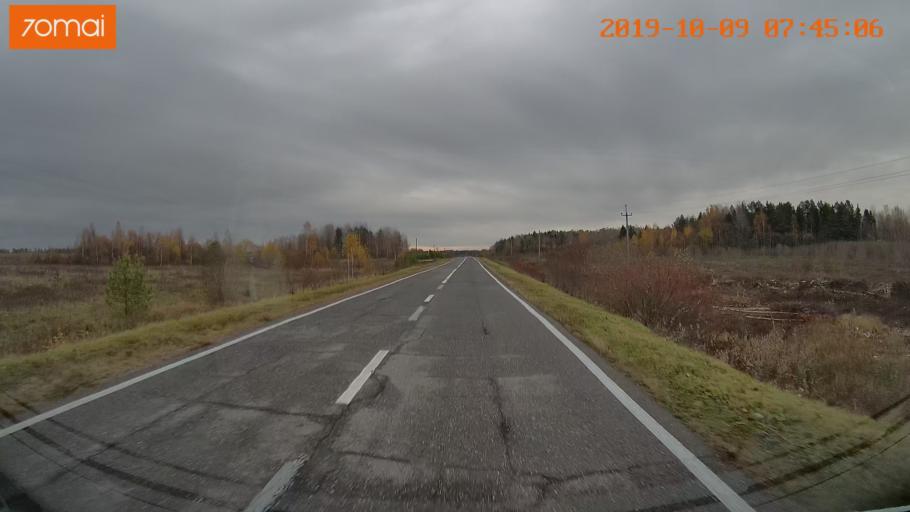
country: RU
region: Jaroslavl
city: Kukoboy
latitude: 58.6522
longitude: 39.7600
